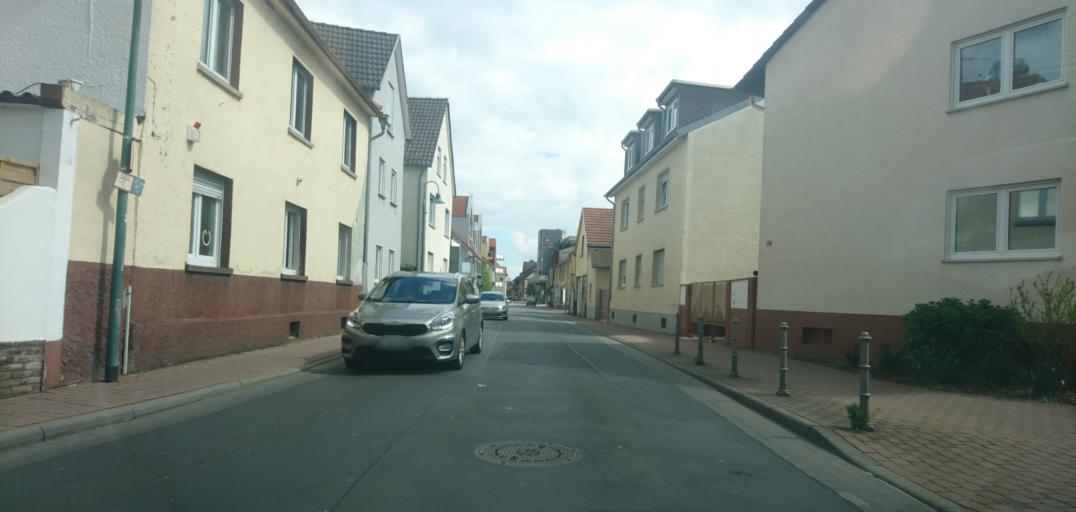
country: DE
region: Hesse
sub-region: Regierungsbezirk Darmstadt
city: Dietzenbach
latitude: 50.0107
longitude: 8.7768
